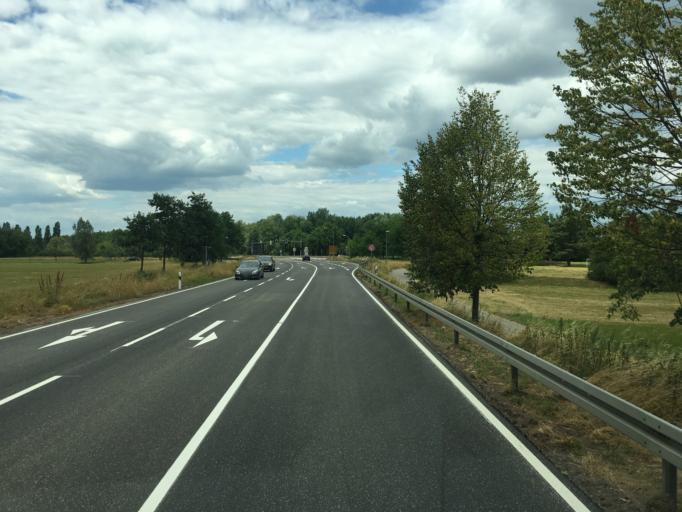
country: DE
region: Baden-Wuerttemberg
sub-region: Karlsruhe Region
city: Ottenhofen
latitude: 48.7293
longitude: 8.1542
